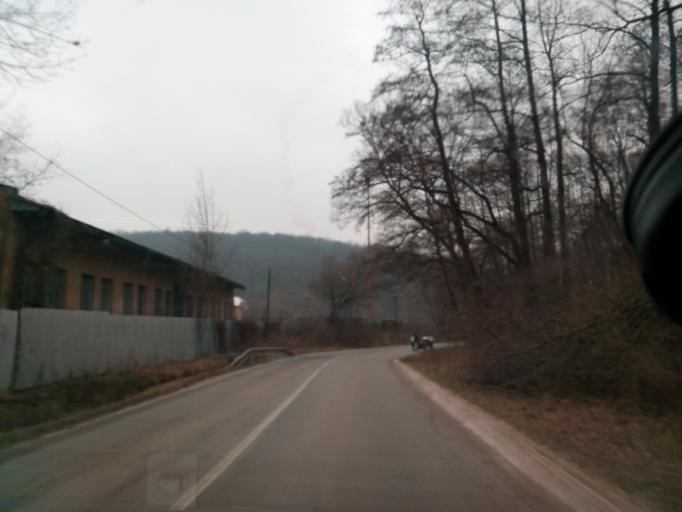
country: SK
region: Kosicky
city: Medzev
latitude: 48.6943
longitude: 20.9441
